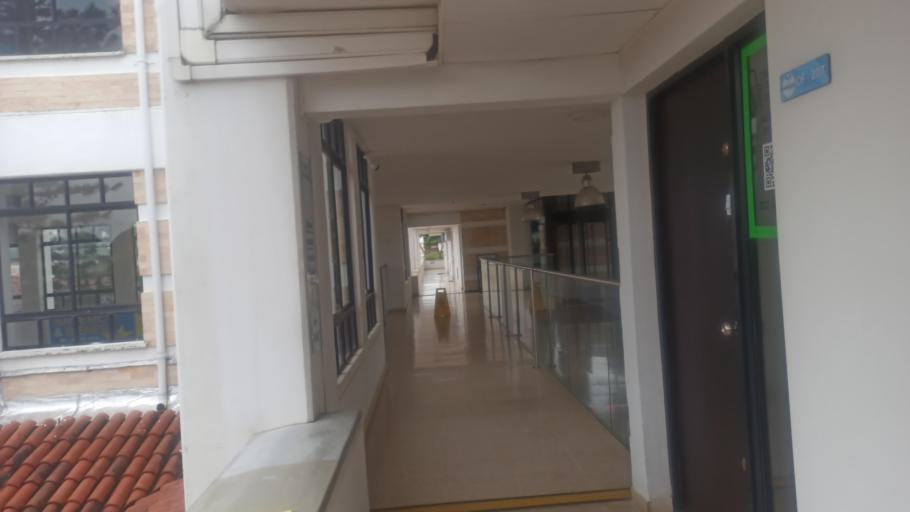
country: CO
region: Valle del Cauca
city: Jamundi
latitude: 3.2588
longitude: -76.5571
